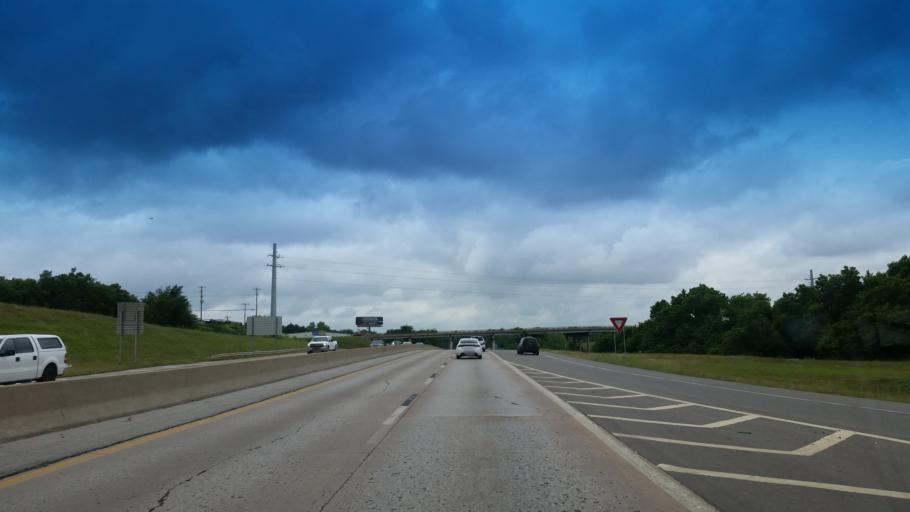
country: US
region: Oklahoma
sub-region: Oklahoma County
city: Nichols Hills
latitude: 35.5249
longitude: -97.5155
